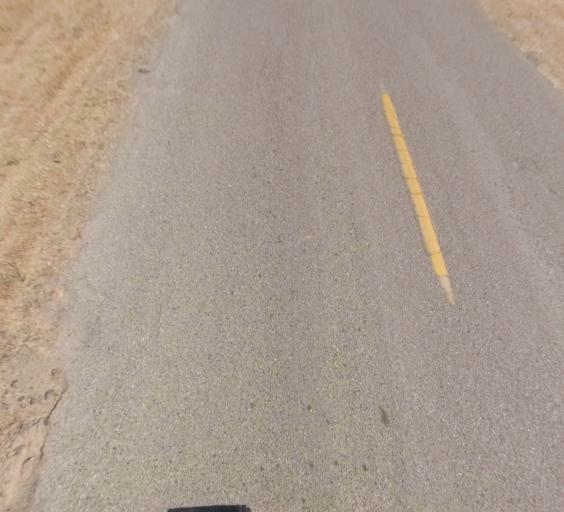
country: US
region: California
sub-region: Madera County
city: Bonadelle Ranchos-Madera Ranchos
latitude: 36.9920
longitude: -119.8865
